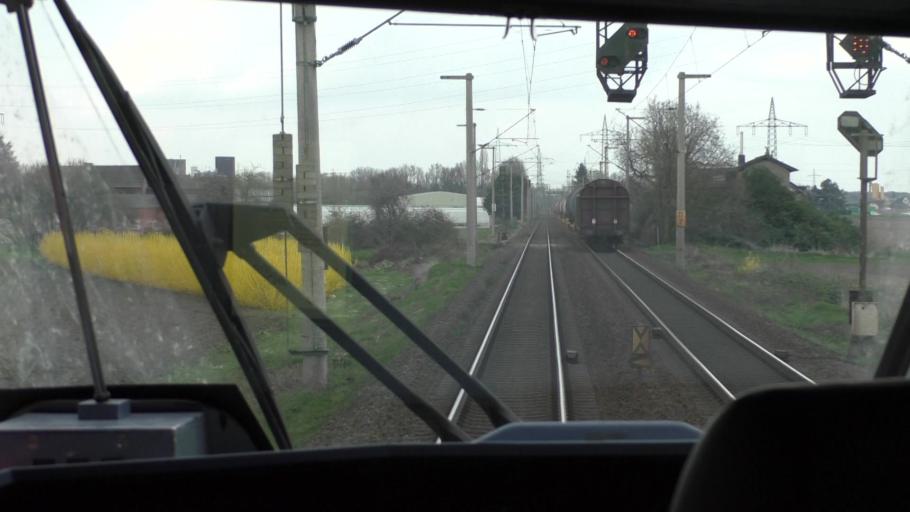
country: DE
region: North Rhine-Westphalia
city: Bruhl
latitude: 50.8585
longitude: 6.9088
